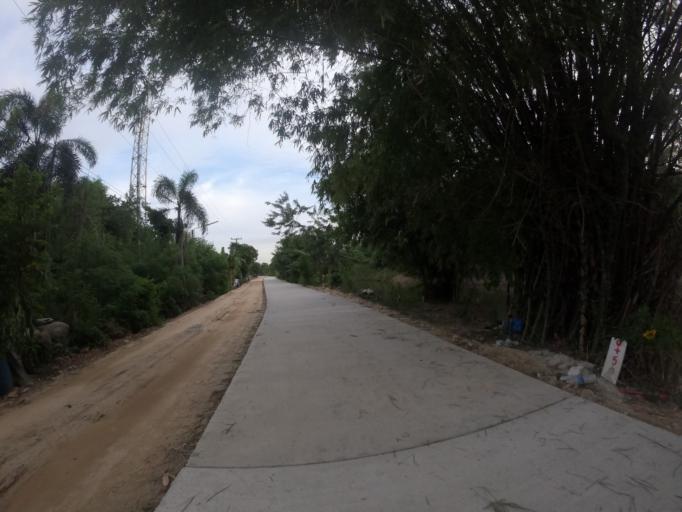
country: TH
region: Pathum Thani
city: Ban Rangsit
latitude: 14.0182
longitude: 100.7997
